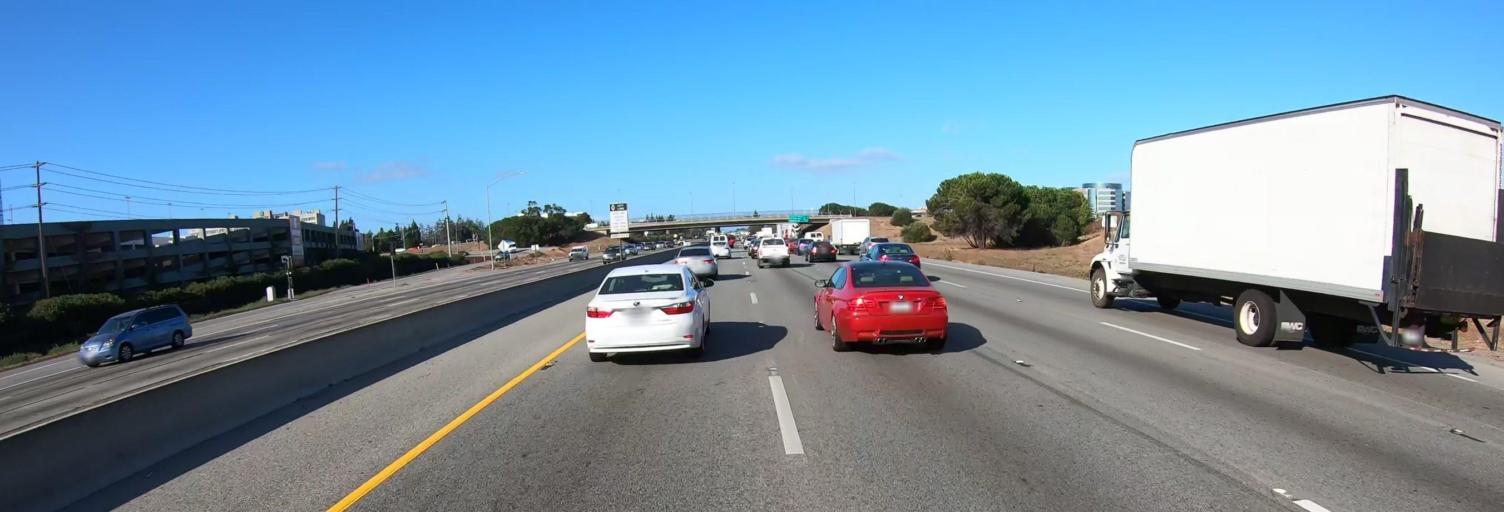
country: US
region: California
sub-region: Santa Clara County
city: Santa Clara
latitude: 37.3841
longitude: -121.9739
